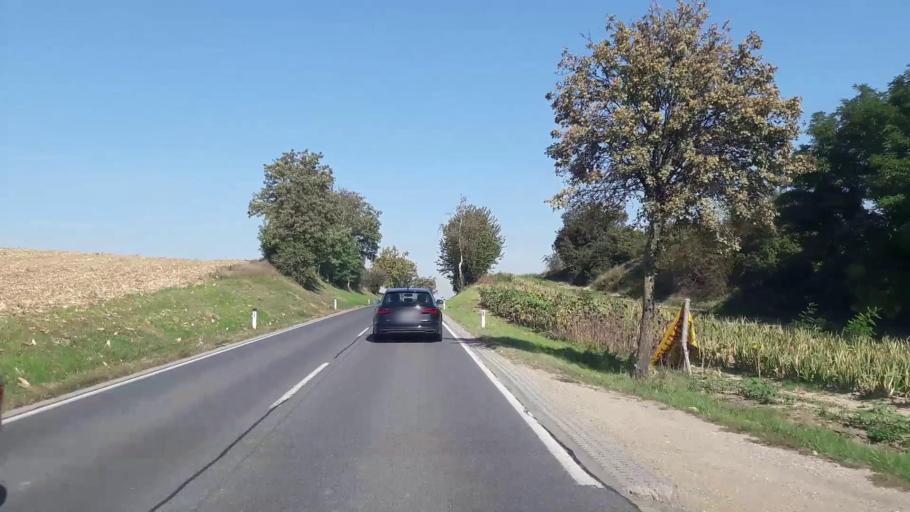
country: AT
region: Lower Austria
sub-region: Politischer Bezirk Korneuburg
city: Harmannsdorf
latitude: 48.3687
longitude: 16.3573
